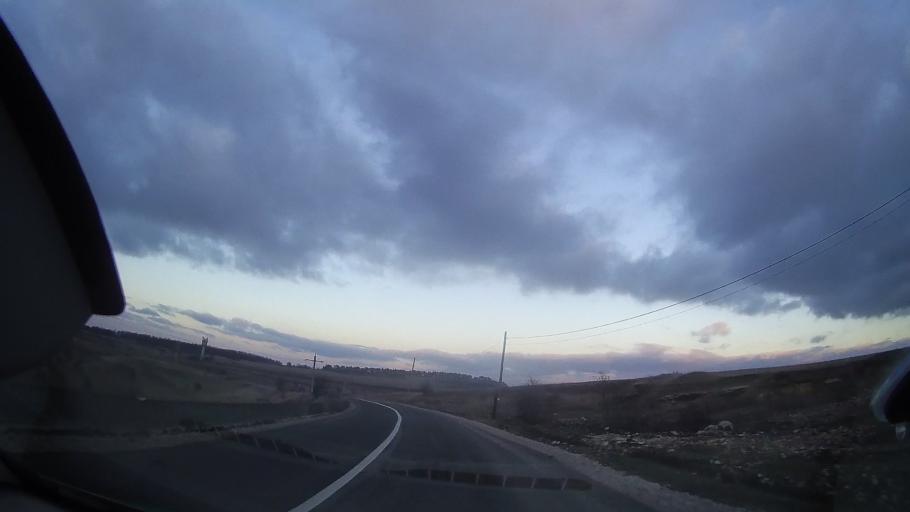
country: RO
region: Cluj
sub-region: Comuna Izvoru Crisului
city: Izvoru Crisului
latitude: 46.8200
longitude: 23.1521
